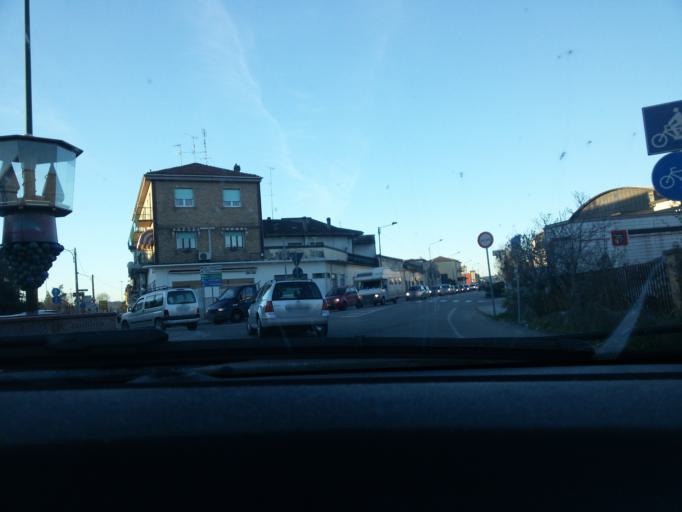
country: IT
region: Piedmont
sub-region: Provincia di Alessandria
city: Casale Monferrato
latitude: 45.1205
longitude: 8.4510
